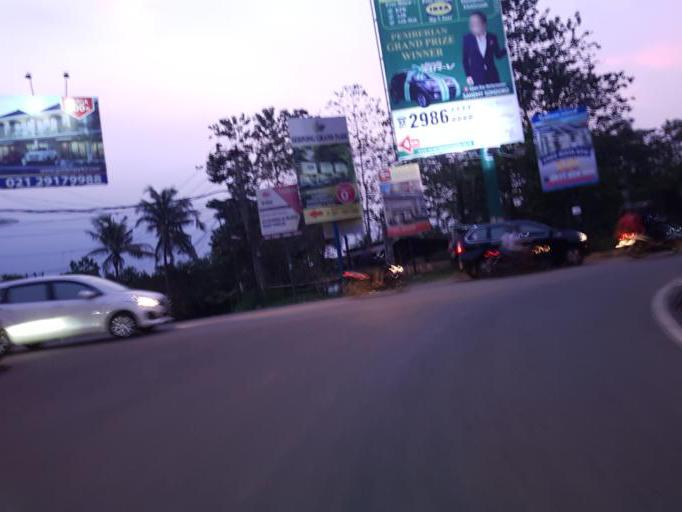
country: ID
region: West Java
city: Serpong
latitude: -6.3314
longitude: 106.6739
